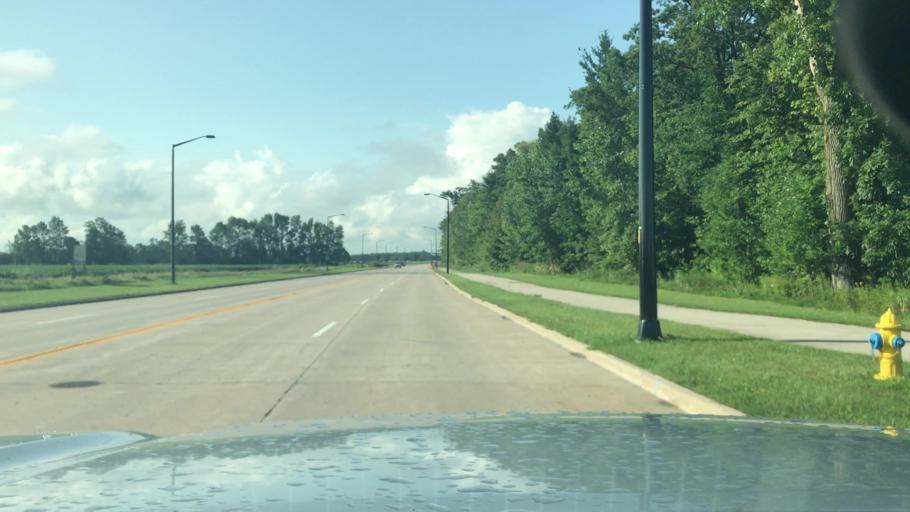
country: US
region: Wisconsin
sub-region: Brown County
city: Bellevue
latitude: 44.4763
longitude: -87.9173
